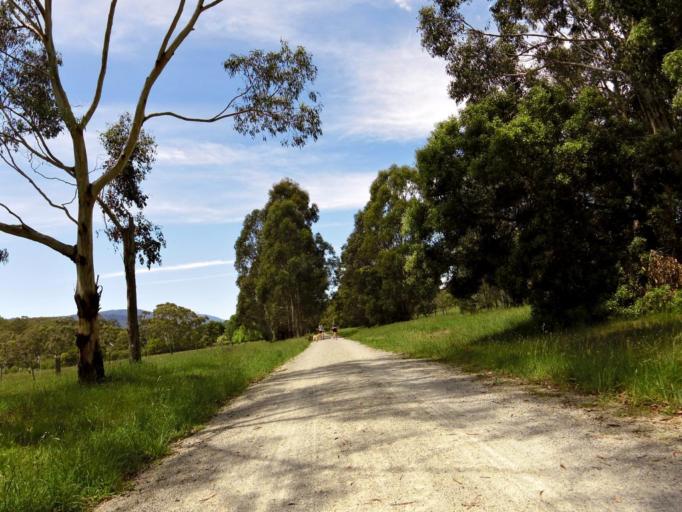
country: AU
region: Victoria
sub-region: Yarra Ranges
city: Woori Yallock
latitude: -37.7579
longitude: 145.4879
